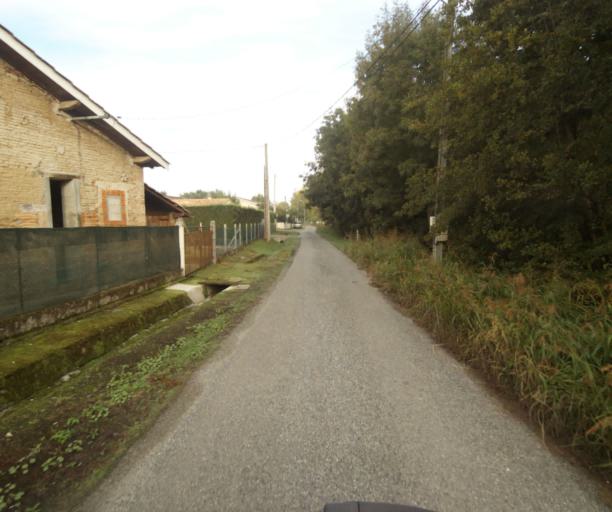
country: FR
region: Midi-Pyrenees
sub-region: Departement du Tarn-et-Garonne
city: Montech
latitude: 43.9641
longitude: 1.2325
